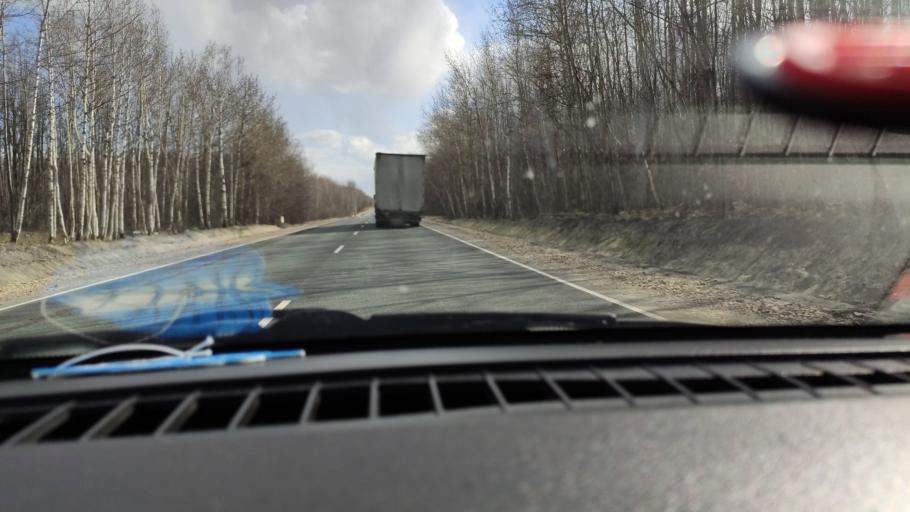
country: RU
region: Saratov
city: Khvalynsk
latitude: 52.4295
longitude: 48.0087
